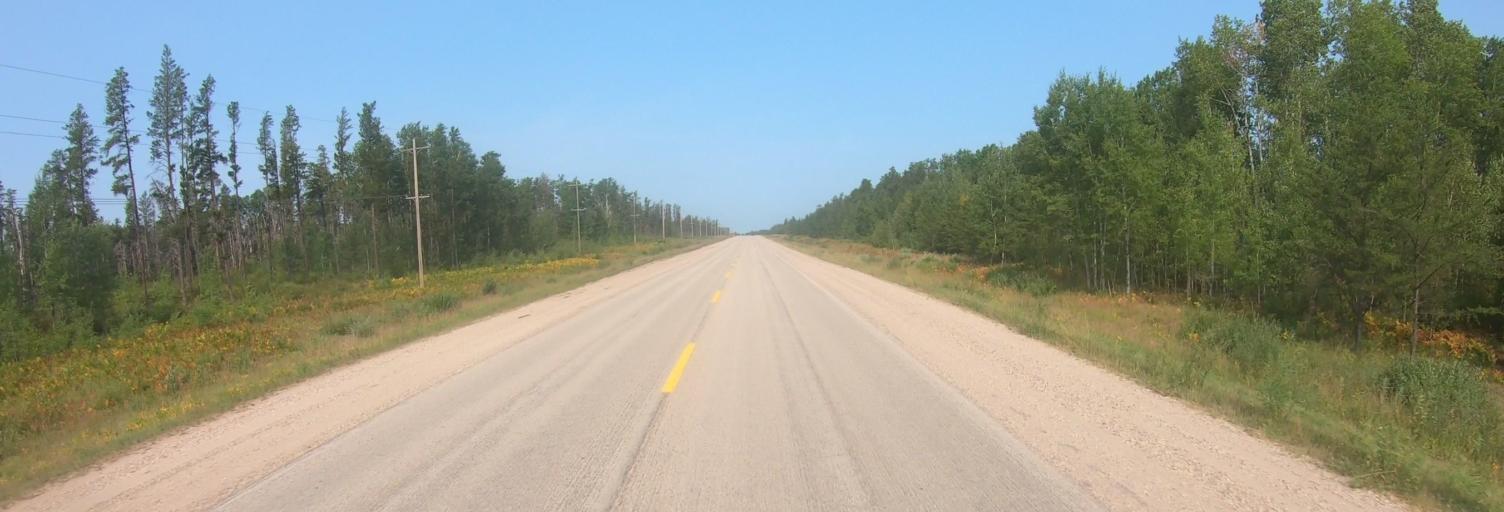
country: US
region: Minnesota
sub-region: Roseau County
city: Roseau
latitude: 49.0806
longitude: -95.8706
